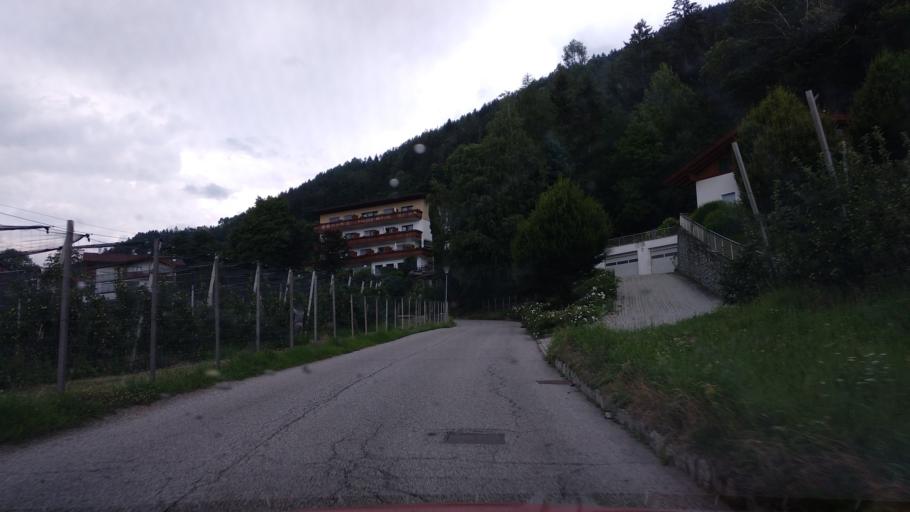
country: IT
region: Trentino-Alto Adige
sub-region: Bolzano
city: Scena
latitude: 46.6963
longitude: 11.2006
